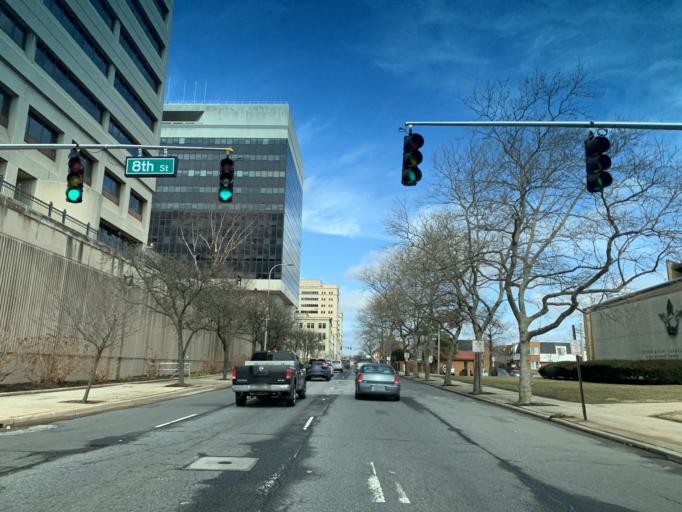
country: US
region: Delaware
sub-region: New Castle County
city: Wilmington
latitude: 39.7423
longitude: -75.5465
